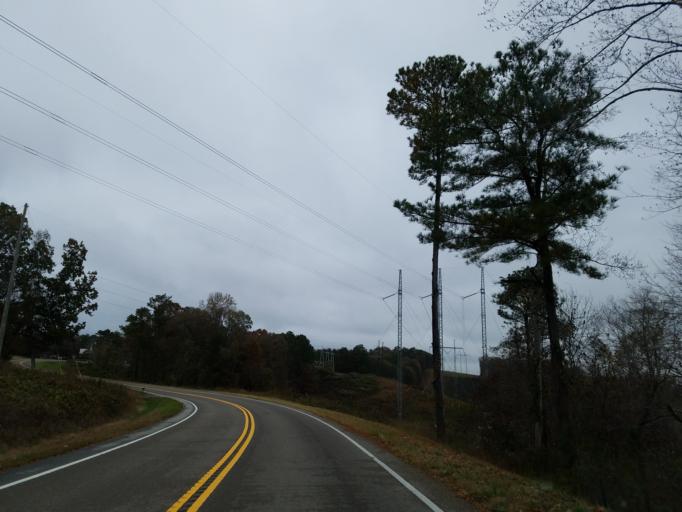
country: US
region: Georgia
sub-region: Cherokee County
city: Canton
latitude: 34.2727
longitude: -84.5811
